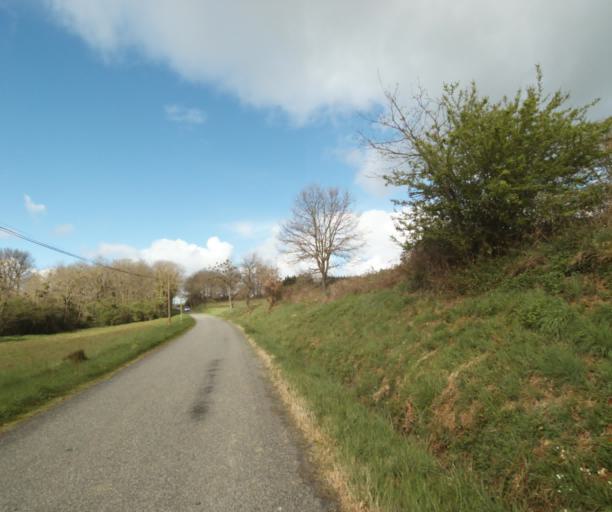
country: FR
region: Midi-Pyrenees
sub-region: Departement de l'Ariege
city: Saverdun
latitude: 43.2324
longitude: 1.5551
